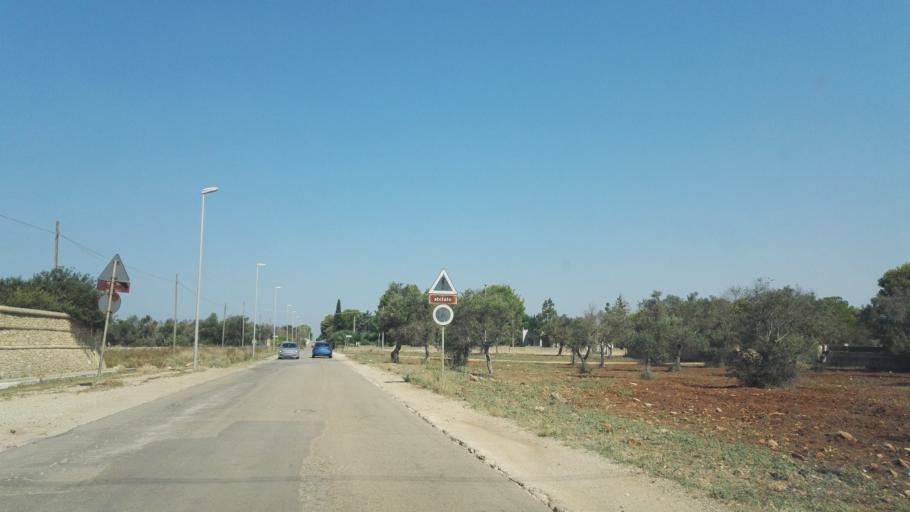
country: IT
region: Apulia
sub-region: Provincia di Lecce
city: Nardo
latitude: 40.1412
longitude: 18.0125
